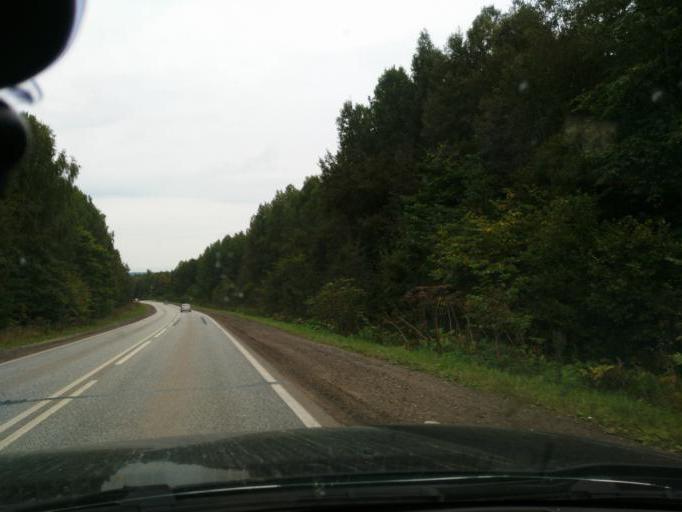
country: RU
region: Perm
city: Chernushka
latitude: 56.5920
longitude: 56.1554
